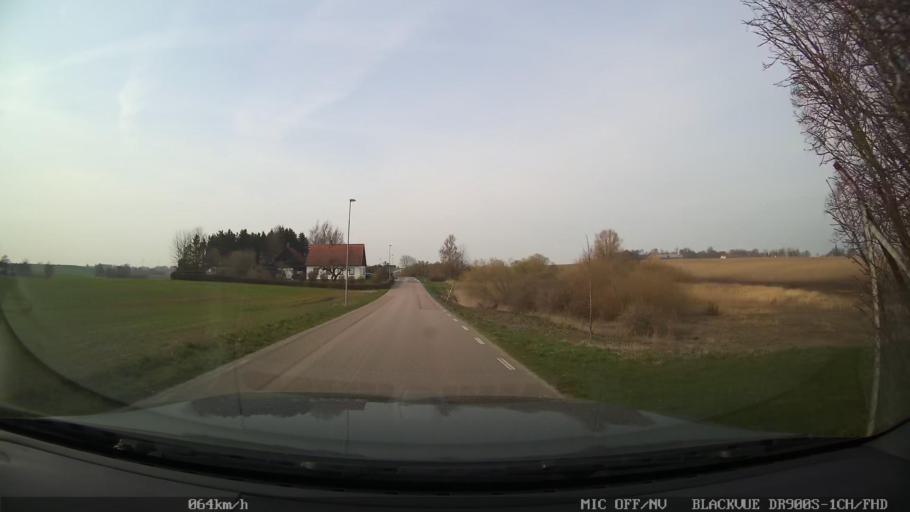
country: SE
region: Skane
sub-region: Ystads Kommun
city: Ystad
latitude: 55.4462
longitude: 13.8338
